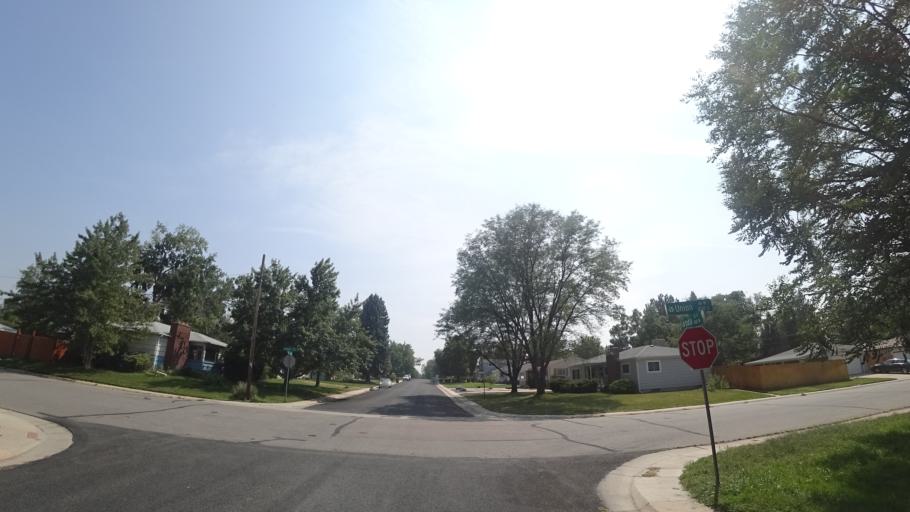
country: US
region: Colorado
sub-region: Arapahoe County
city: Englewood
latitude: 39.6315
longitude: -104.9985
